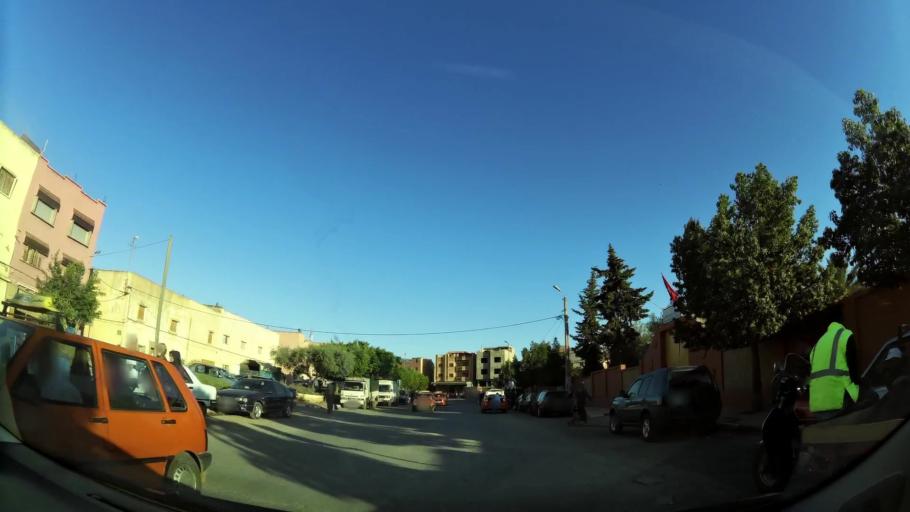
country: MA
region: Oriental
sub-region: Berkane-Taourirt
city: Berkane
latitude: 34.9228
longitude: -2.3175
